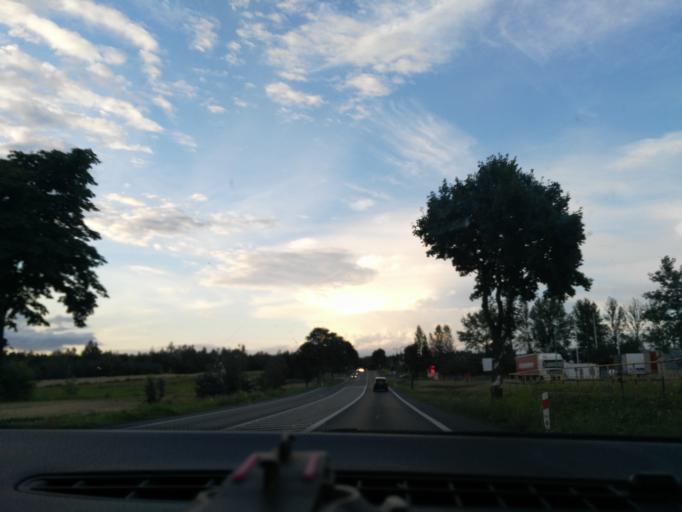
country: PL
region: Lublin Voivodeship
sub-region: Powiat lubelski
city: Niemce
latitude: 51.3693
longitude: 22.6323
